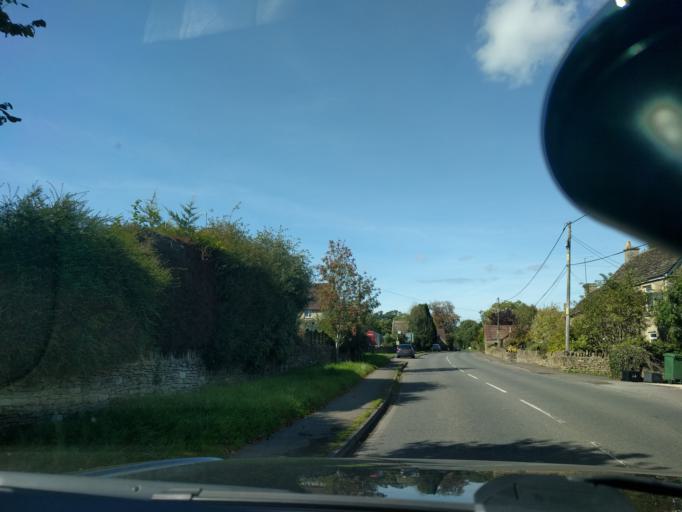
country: GB
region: England
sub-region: Wiltshire
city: Corsham
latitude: 51.4160
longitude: -2.1684
